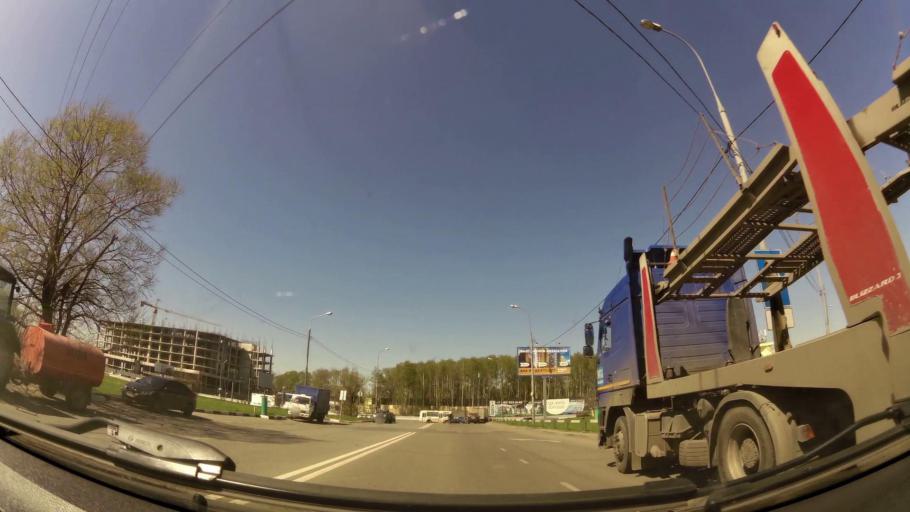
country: RU
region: Moscow
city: Strogino
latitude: 55.8016
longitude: 37.3861
